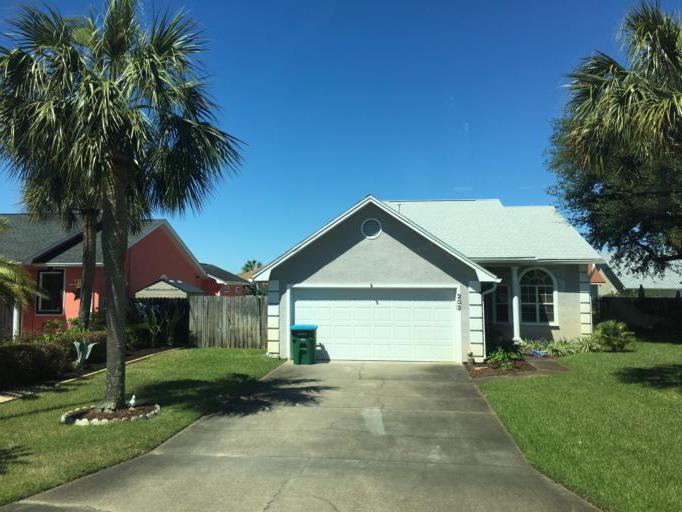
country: US
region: Florida
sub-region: Bay County
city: Panama City Beach
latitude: 30.2075
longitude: -85.8477
